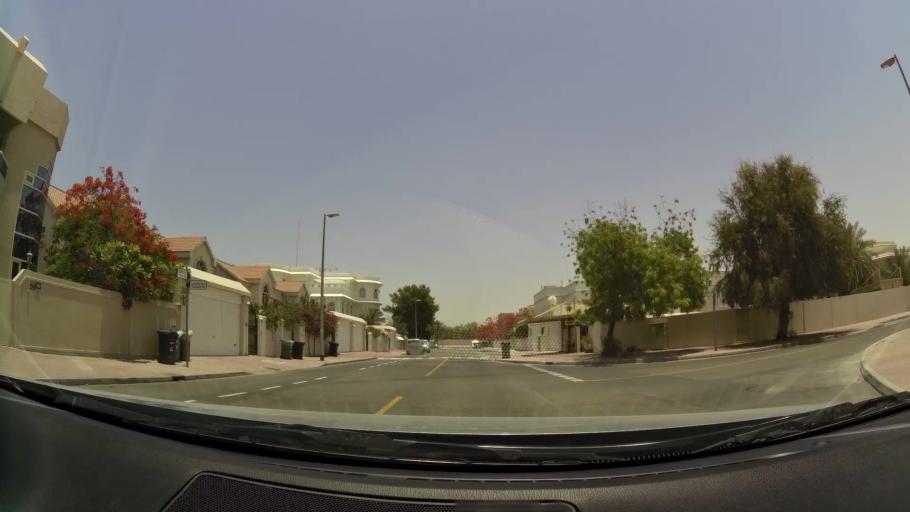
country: AE
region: Dubai
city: Dubai
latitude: 25.1737
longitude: 55.2242
